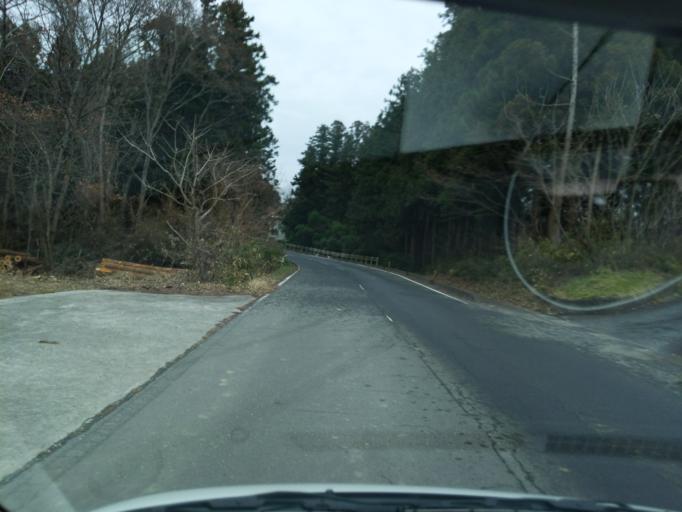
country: JP
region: Iwate
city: Ichinoseki
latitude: 38.7387
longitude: 141.2509
